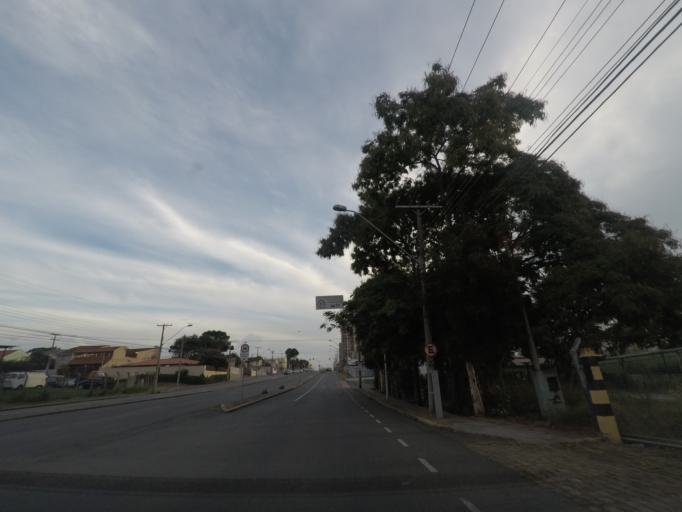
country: BR
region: Parana
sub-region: Curitiba
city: Curitiba
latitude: -25.3818
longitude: -49.2298
